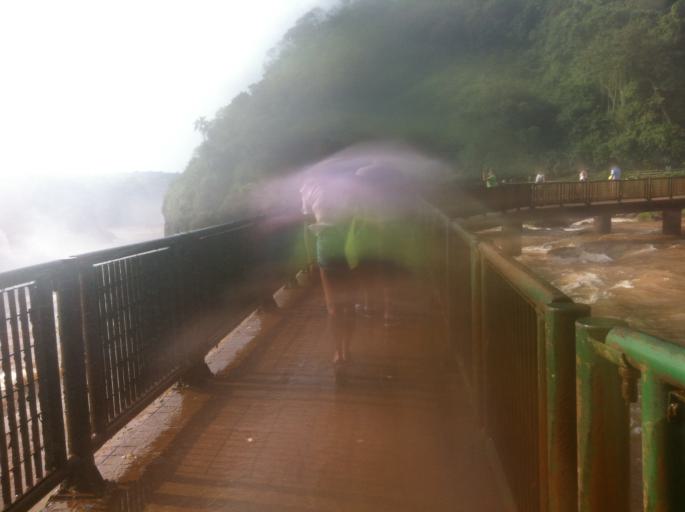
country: AR
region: Misiones
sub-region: Departamento de Iguazu
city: Puerto Iguazu
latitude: -25.6914
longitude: -54.4379
